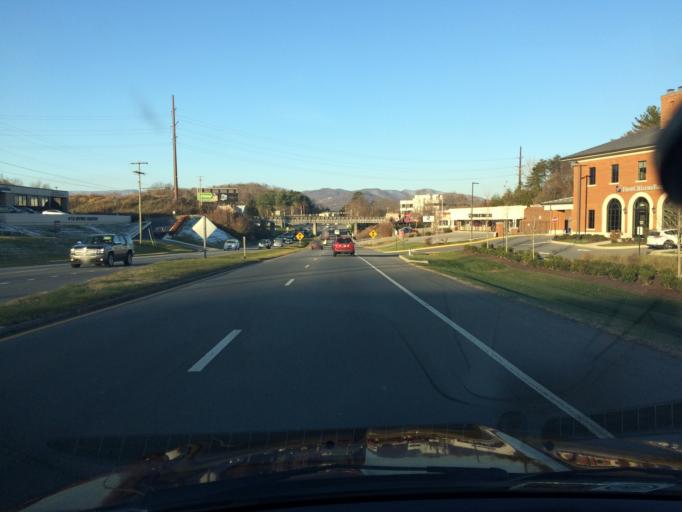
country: US
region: Virginia
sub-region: Roanoke County
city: Cave Spring
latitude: 37.2240
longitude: -79.9873
